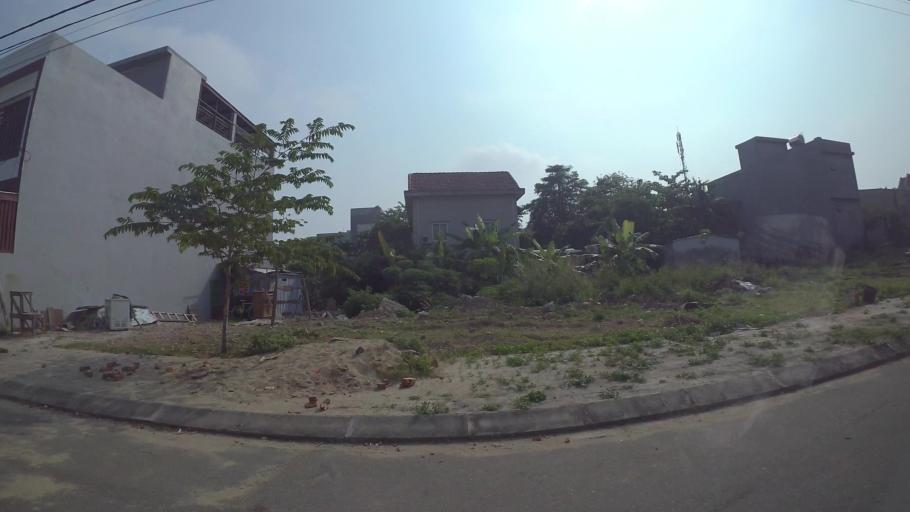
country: VN
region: Da Nang
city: Ngu Hanh Son
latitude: 16.0288
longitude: 108.2437
